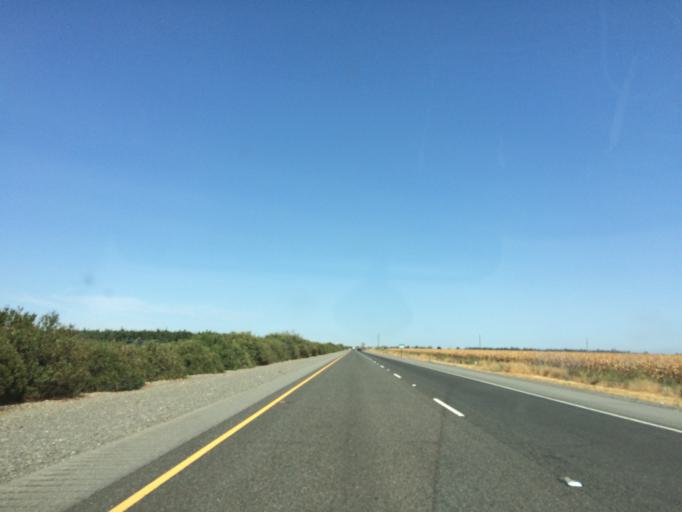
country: US
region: California
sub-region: Glenn County
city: Willows
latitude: 39.5481
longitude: -122.2147
